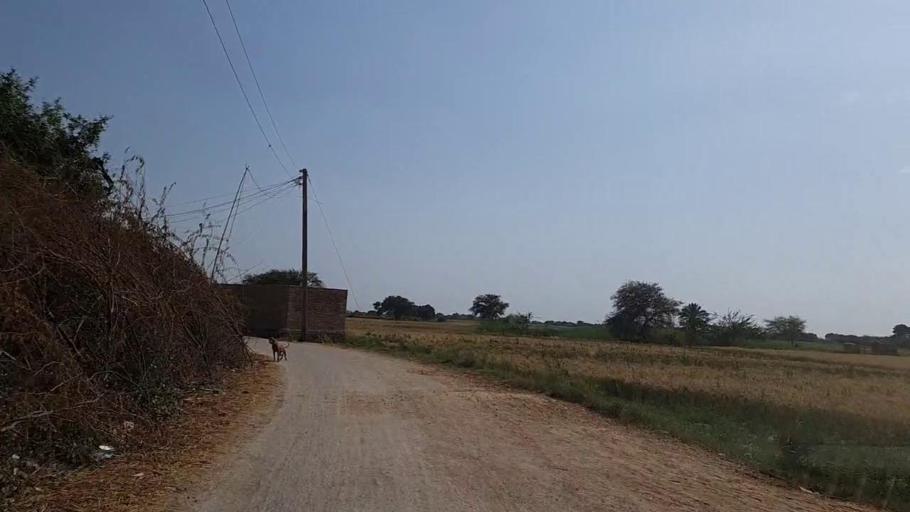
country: PK
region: Sindh
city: Daro Mehar
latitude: 24.7908
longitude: 68.1782
